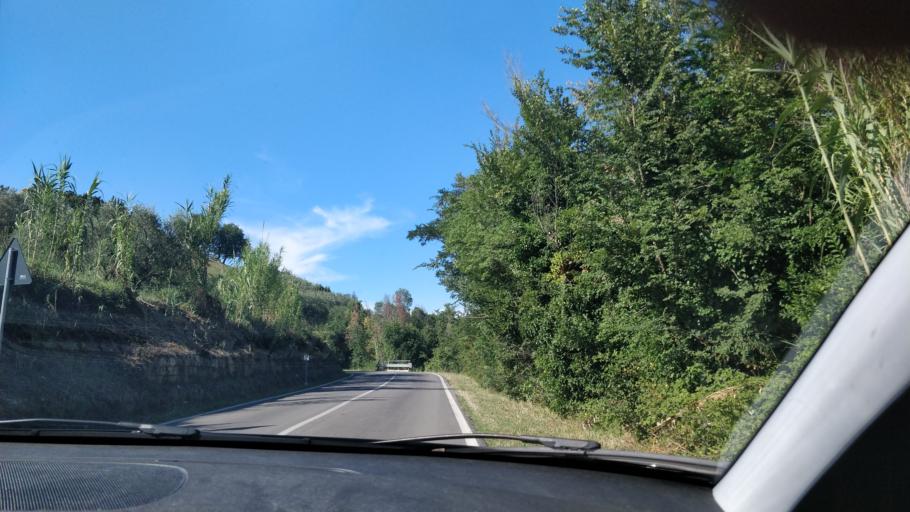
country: IT
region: Abruzzo
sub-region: Provincia di Pescara
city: Serramonacesca
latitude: 42.2474
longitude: 14.0888
